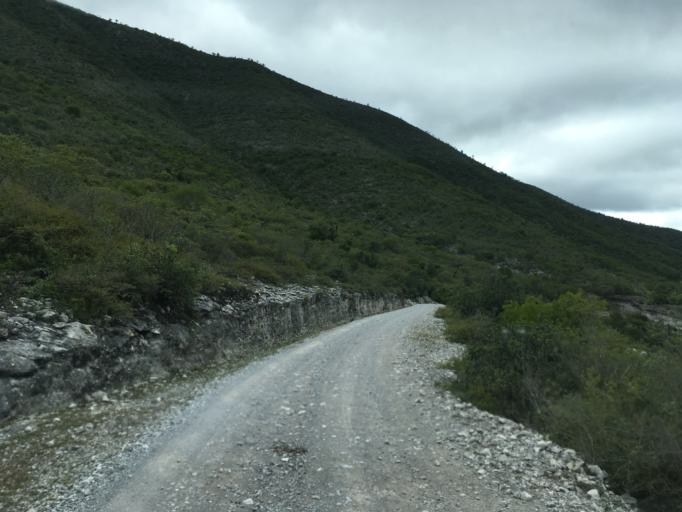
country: MX
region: Hidalgo
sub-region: Metztitlan
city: Fontezuelas
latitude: 20.6233
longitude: -98.8657
